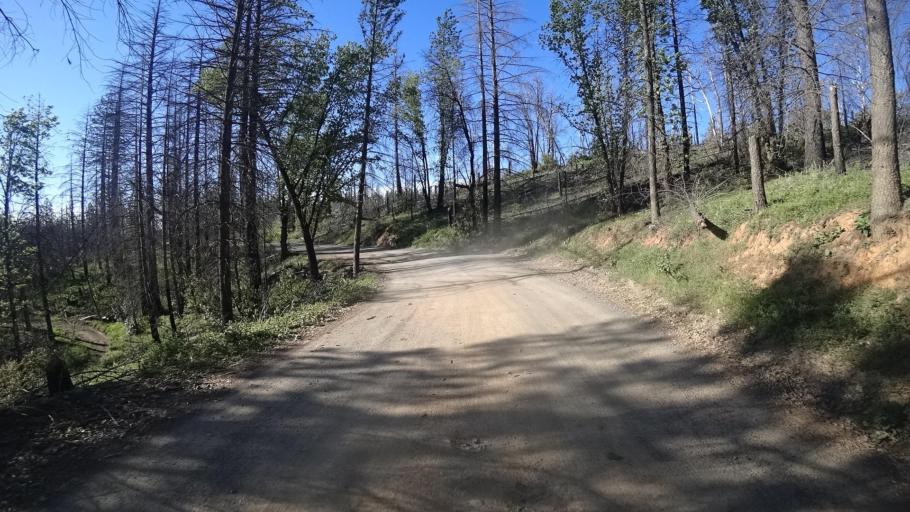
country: US
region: California
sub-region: Lake County
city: Upper Lake
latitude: 39.3379
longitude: -122.9577
